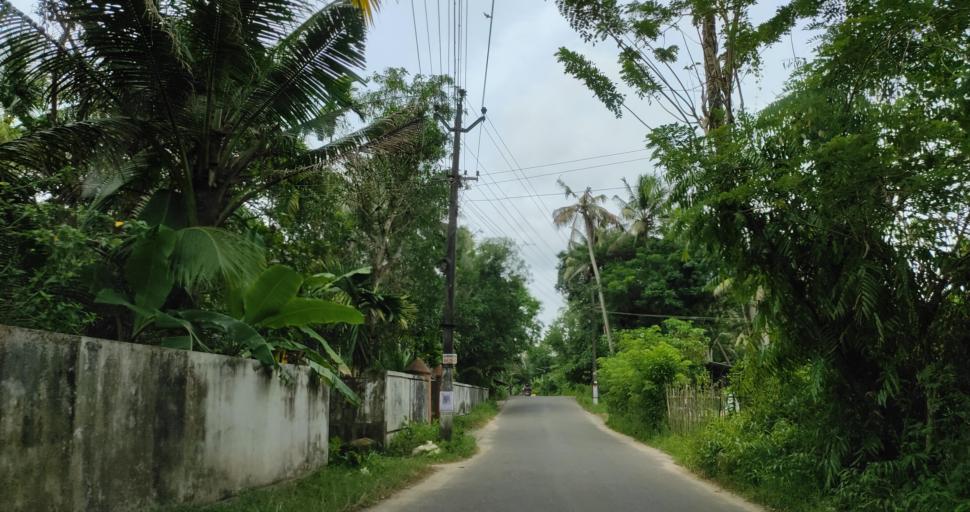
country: IN
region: Kerala
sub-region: Alappuzha
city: Shertallai
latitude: 9.6724
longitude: 76.3546
